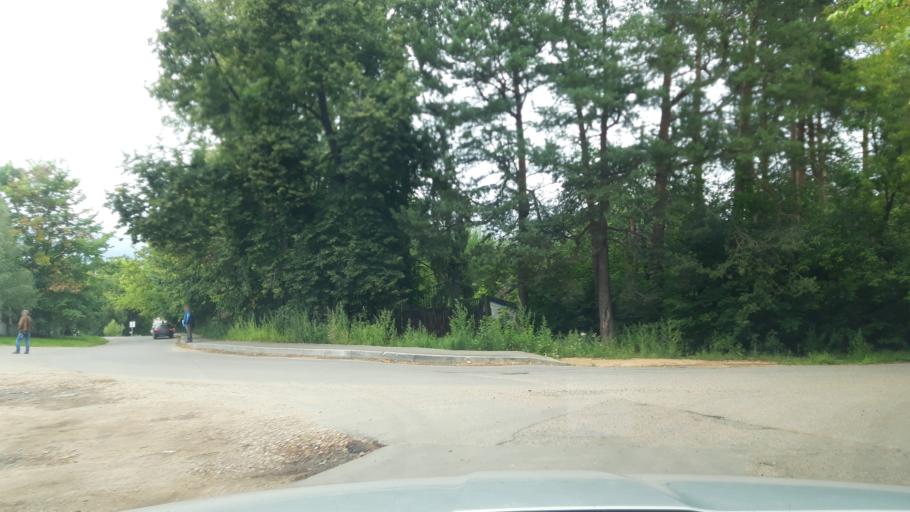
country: RU
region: Moskovskaya
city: Povarovo
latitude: 56.0608
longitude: 37.0590
